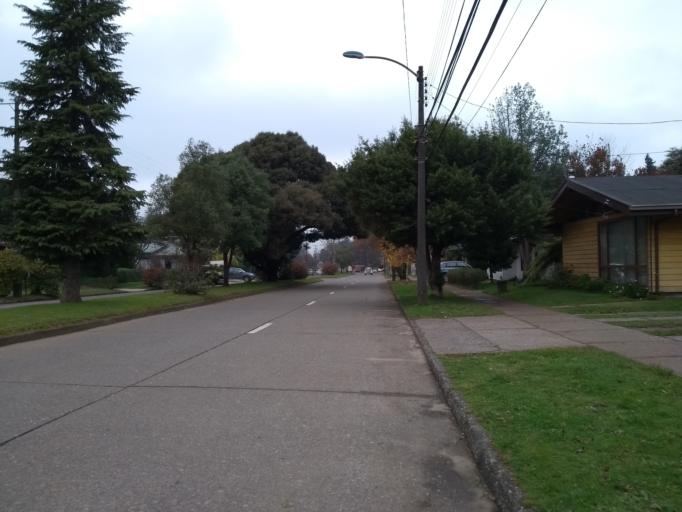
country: CL
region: Los Rios
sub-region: Provincia de Valdivia
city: Valdivia
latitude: -39.8095
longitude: -73.2596
